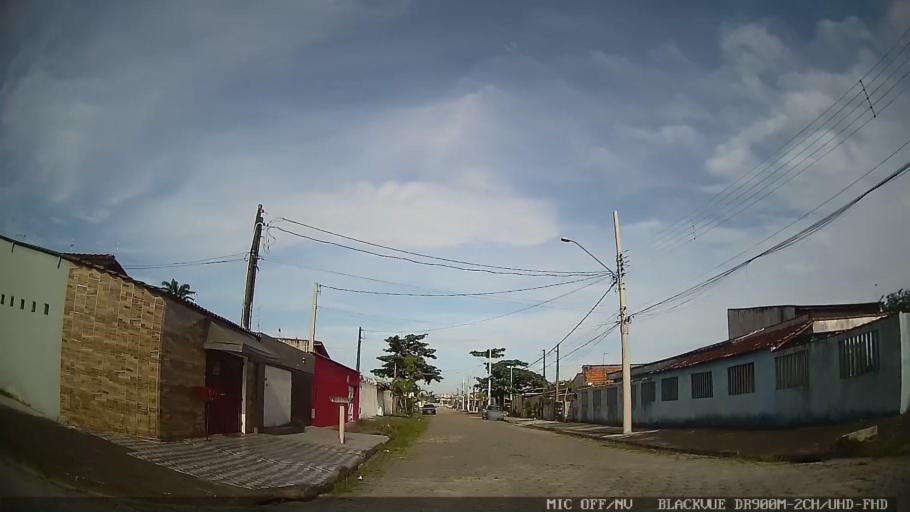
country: BR
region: Sao Paulo
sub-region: Itanhaem
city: Itanhaem
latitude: -24.1641
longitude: -46.7654
